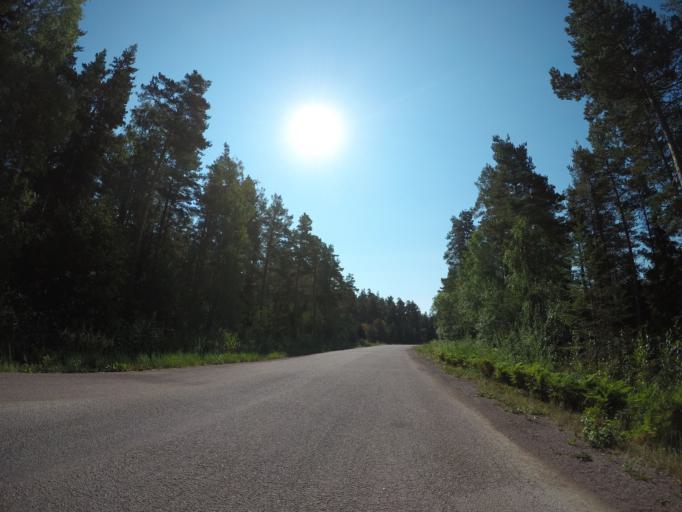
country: AX
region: Alands landsbygd
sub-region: Saltvik
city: Saltvik
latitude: 60.2320
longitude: 20.0056
